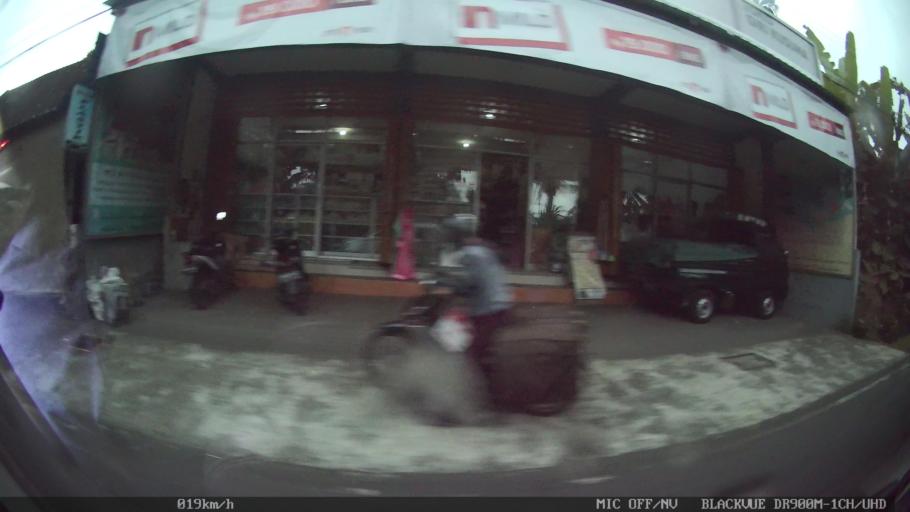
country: ID
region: Bali
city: Banjar Buahan
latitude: -8.4131
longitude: 115.2442
